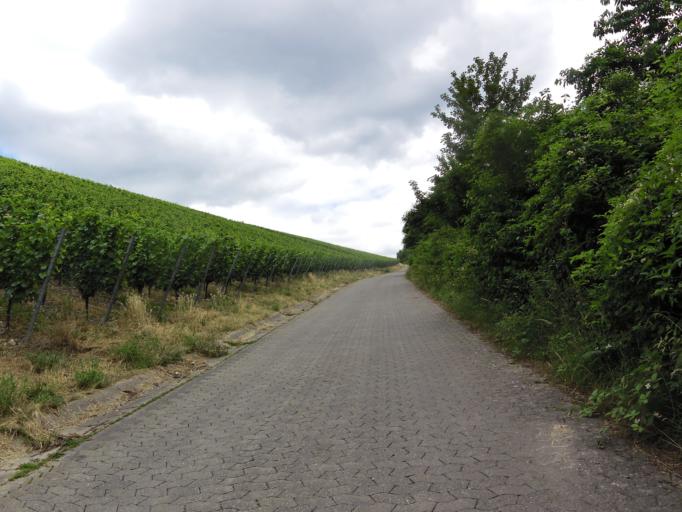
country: DE
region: Bavaria
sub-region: Regierungsbezirk Unterfranken
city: Randersacker
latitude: 49.7663
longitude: 9.9701
